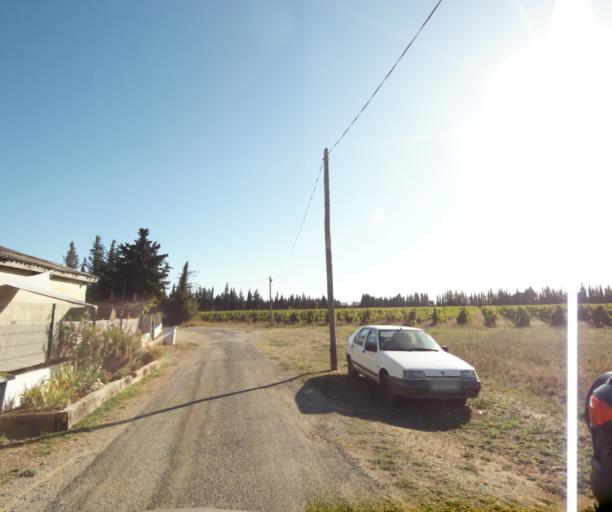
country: FR
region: Languedoc-Roussillon
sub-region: Departement du Gard
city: Bouillargues
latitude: 43.7872
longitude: 4.4602
